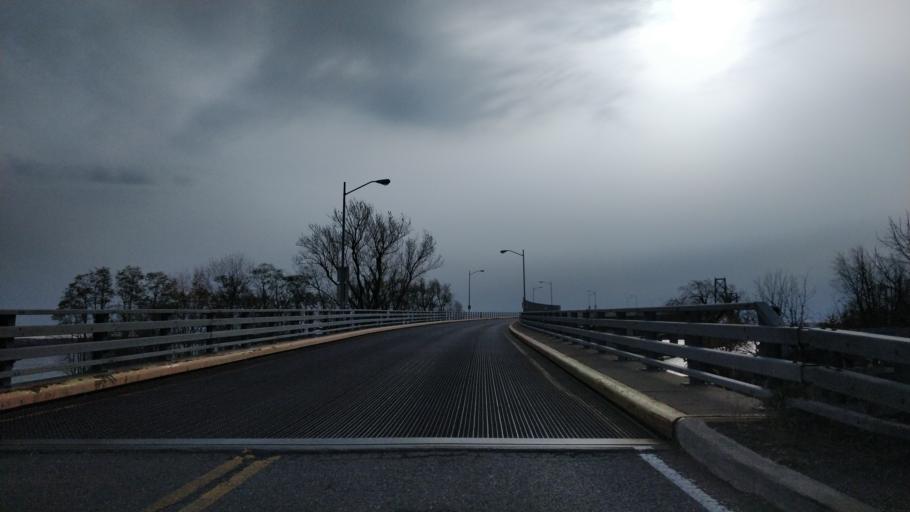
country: US
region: New York
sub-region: St. Lawrence County
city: Ogdensburg
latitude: 44.7440
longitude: -75.4671
